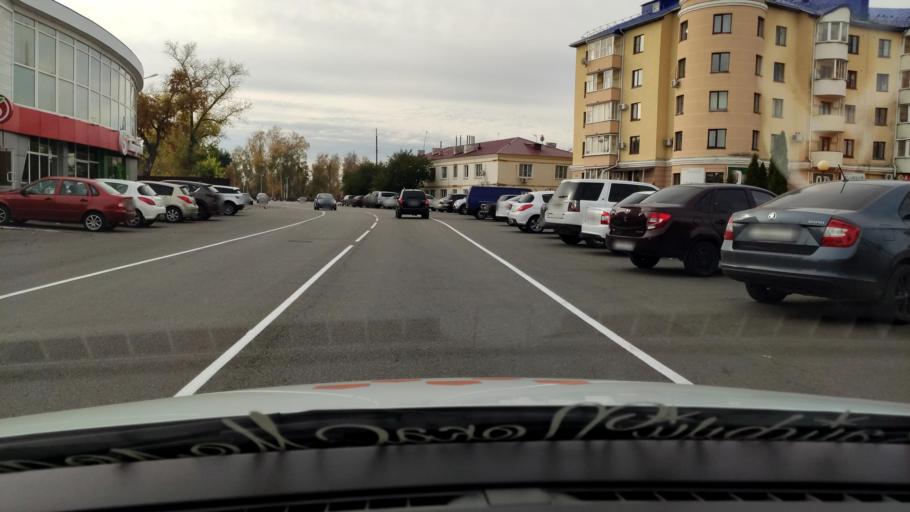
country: RU
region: Voronezj
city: Ramon'
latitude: 51.9126
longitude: 39.3388
